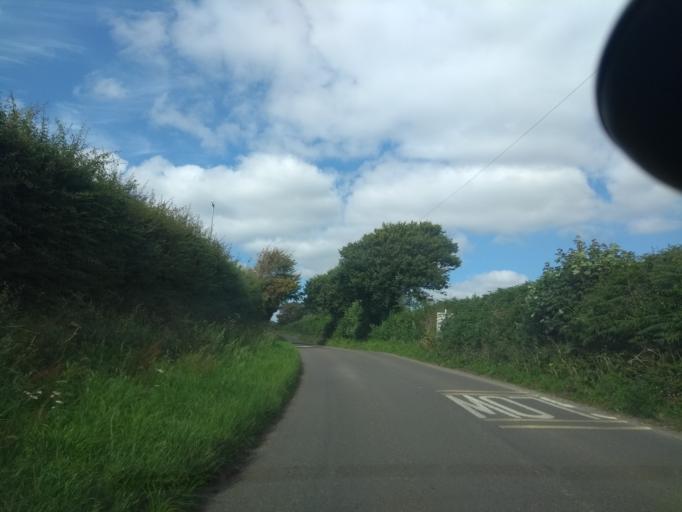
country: GB
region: England
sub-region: Devon
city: Modbury
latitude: 50.2985
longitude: -3.8908
